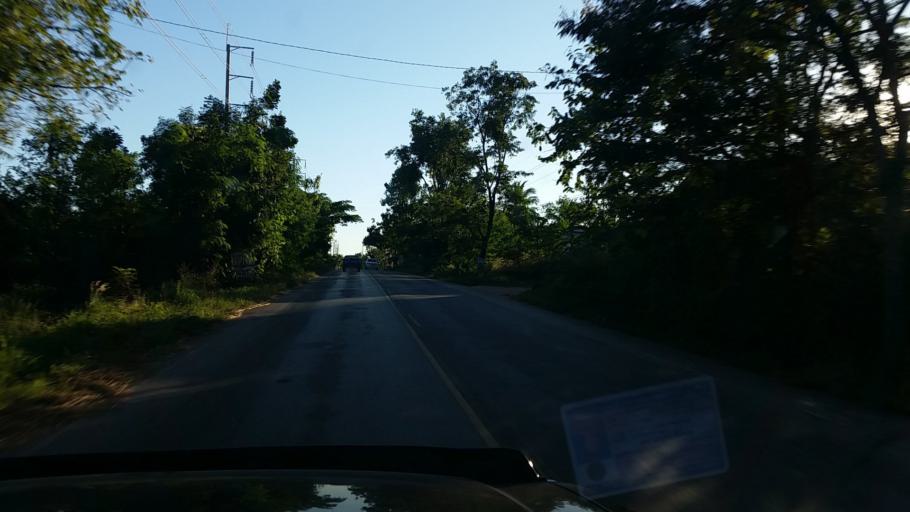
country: TH
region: Chaiyaphum
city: Nong Bua Rawe
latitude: 15.7226
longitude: 101.7435
